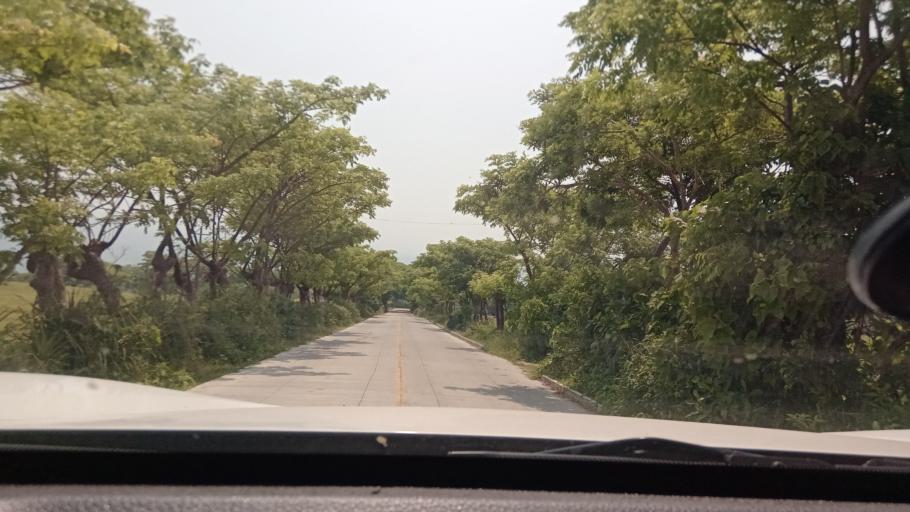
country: MX
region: Veracruz
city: Catemaco
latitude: 18.5606
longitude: -95.0277
